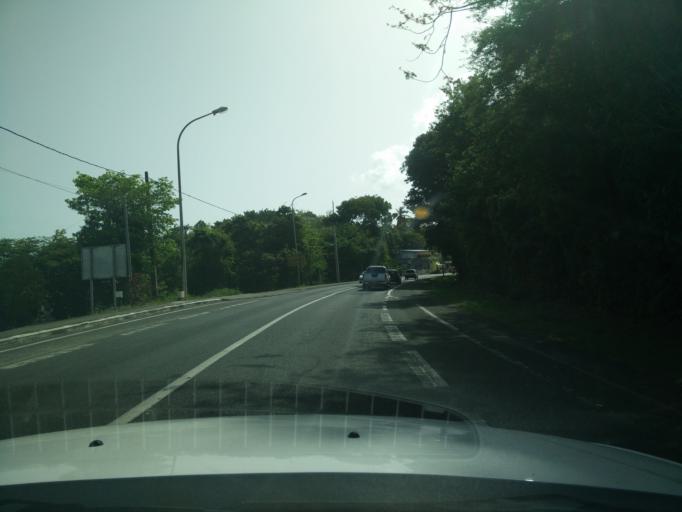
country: GP
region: Guadeloupe
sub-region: Guadeloupe
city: Le Gosier
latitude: 16.2072
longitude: -61.4551
